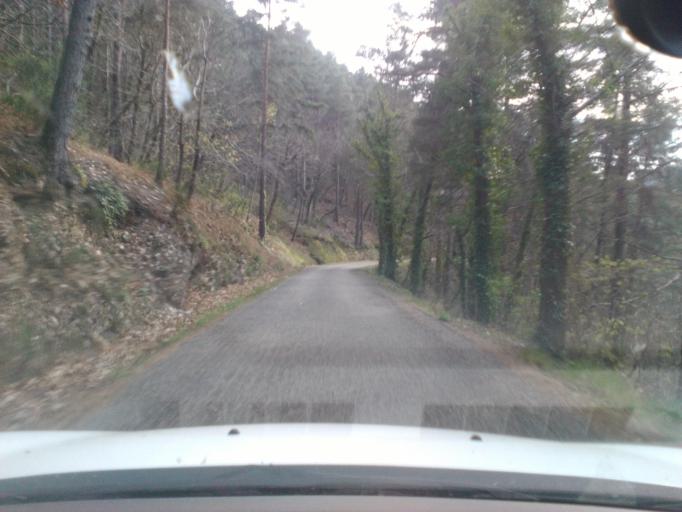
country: FR
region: Languedoc-Roussillon
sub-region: Departement du Gard
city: Saint-Jean-du-Gard
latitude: 44.1359
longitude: 3.7657
